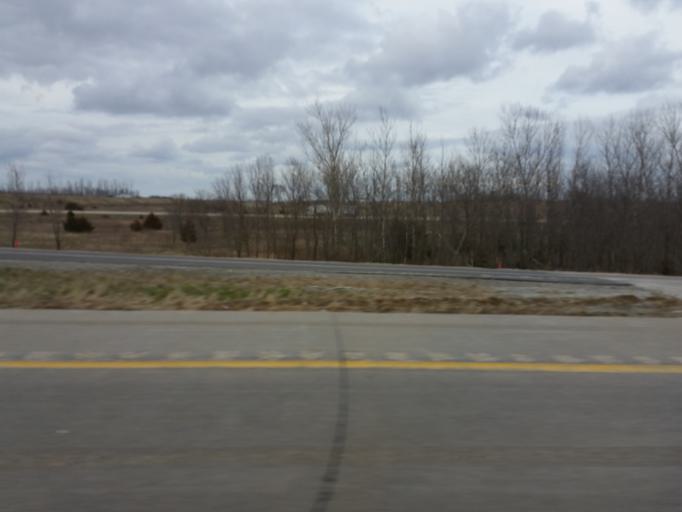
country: US
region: Iowa
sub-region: Black Hawk County
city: Elk Run Heights
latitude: 42.4461
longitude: -92.1927
